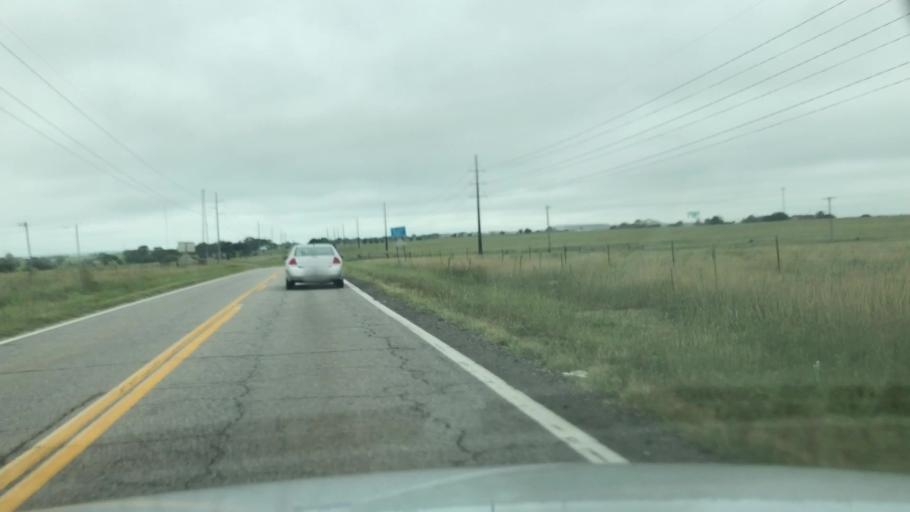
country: US
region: Oklahoma
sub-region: Washington County
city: Dewey
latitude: 36.7280
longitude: -95.8800
